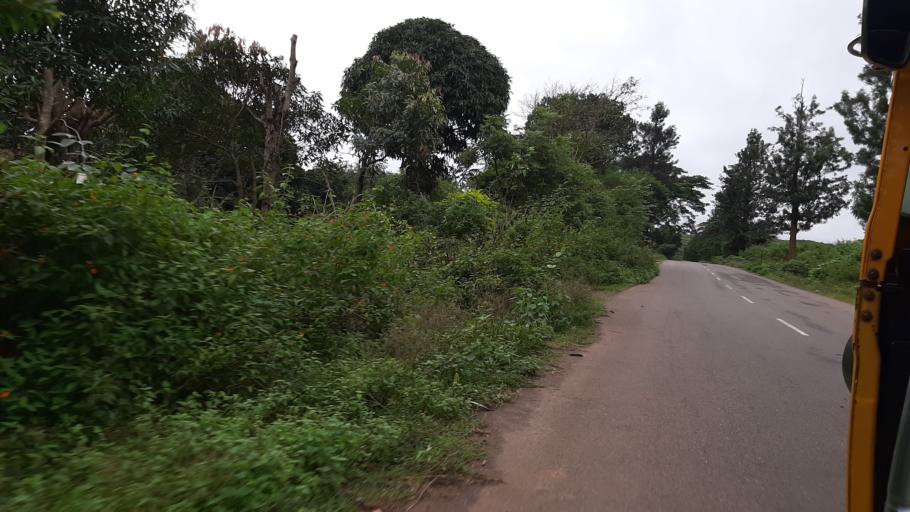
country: IN
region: Andhra Pradesh
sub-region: Vizianagaram District
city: Salur
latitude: 18.3005
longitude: 82.9111
